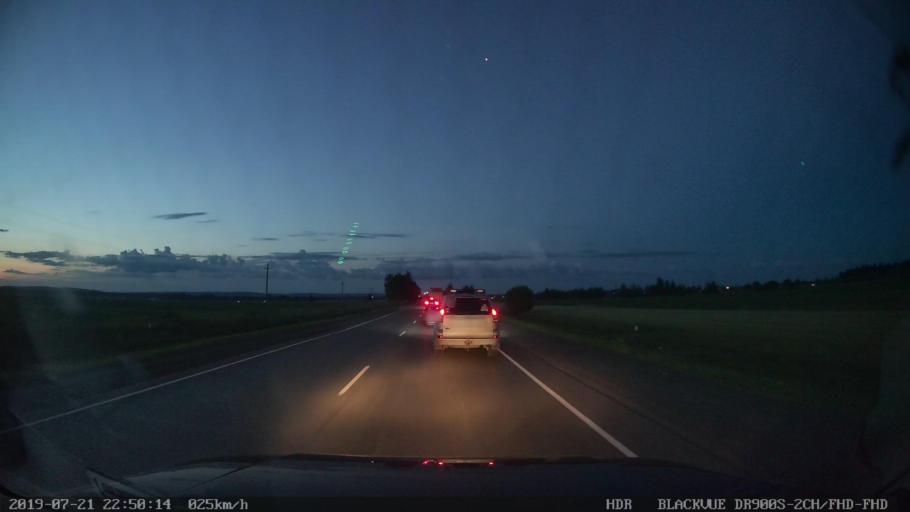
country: RU
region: Perm
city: Ust'-Kachka
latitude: 58.0644
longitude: 55.6200
